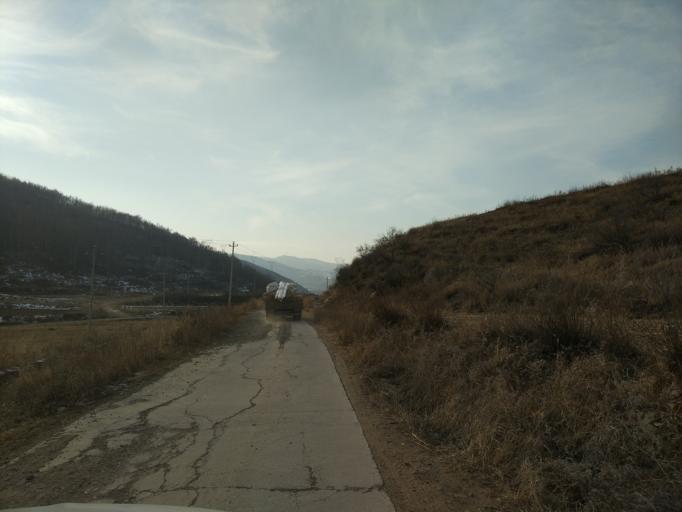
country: CN
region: Hebei
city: Xiwanzi
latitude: 40.8182
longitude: 115.4818
